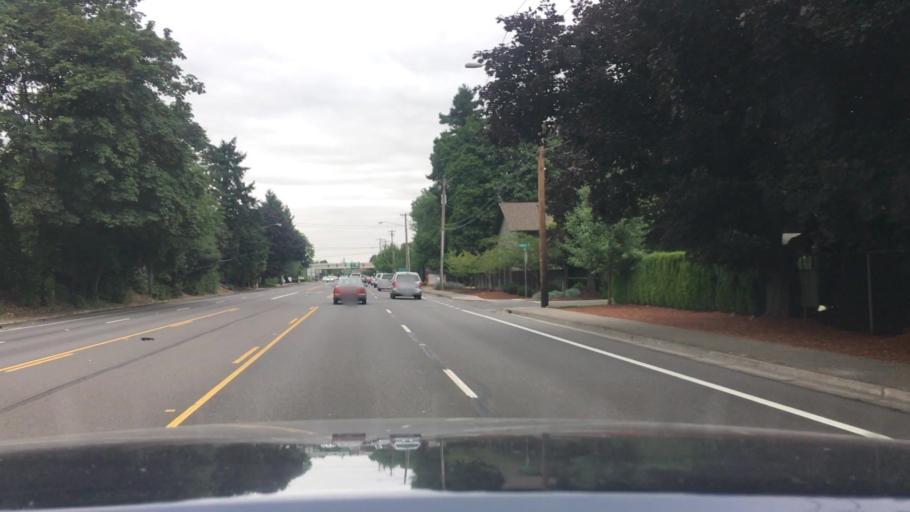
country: US
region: Oregon
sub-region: Lane County
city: Eugene
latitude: 44.0837
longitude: -123.0675
